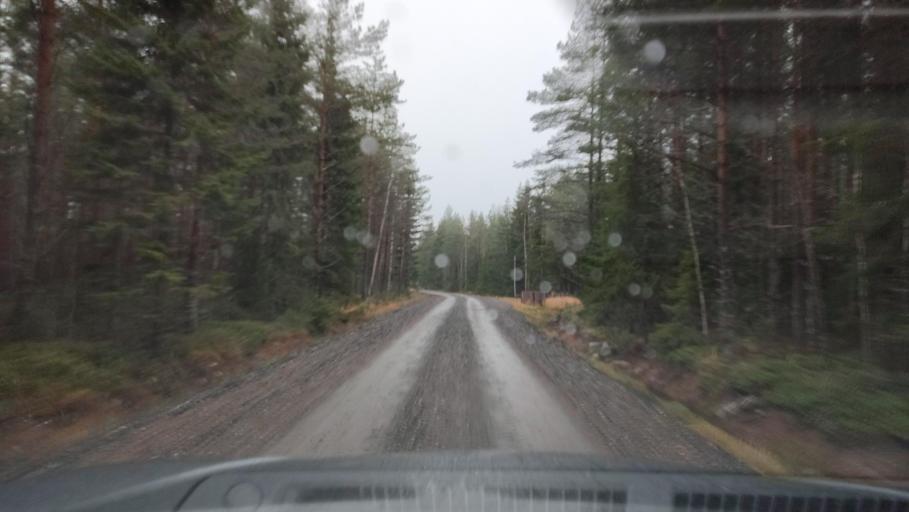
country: FI
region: Southern Ostrobothnia
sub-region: Suupohja
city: Karijoki
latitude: 62.1765
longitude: 21.6986
